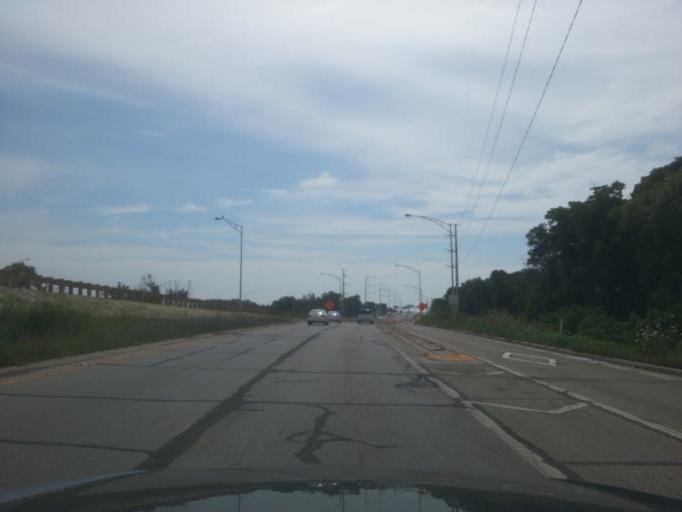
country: US
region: Wisconsin
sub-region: Dane County
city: Shorewood Hills
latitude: 43.0456
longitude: -89.4722
